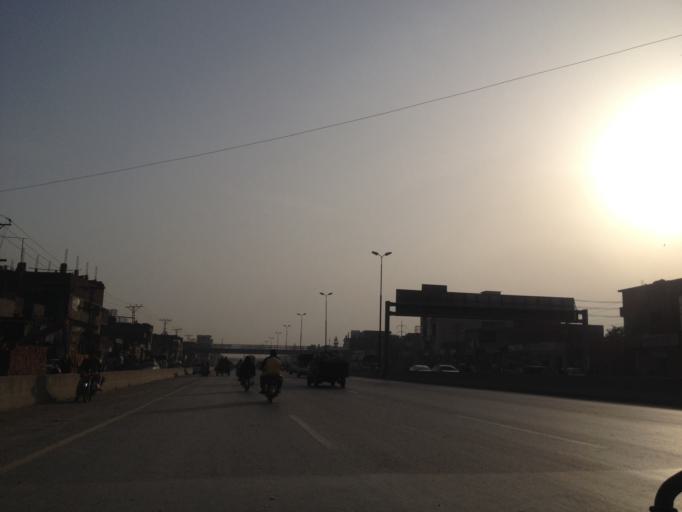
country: PK
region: Punjab
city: Lahore
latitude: 31.5677
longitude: 74.2826
